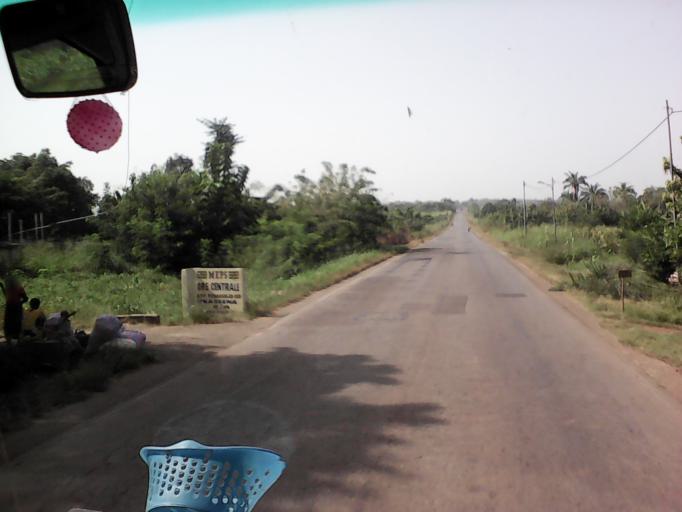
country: TG
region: Centrale
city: Sokode
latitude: 8.8821
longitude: 1.0848
